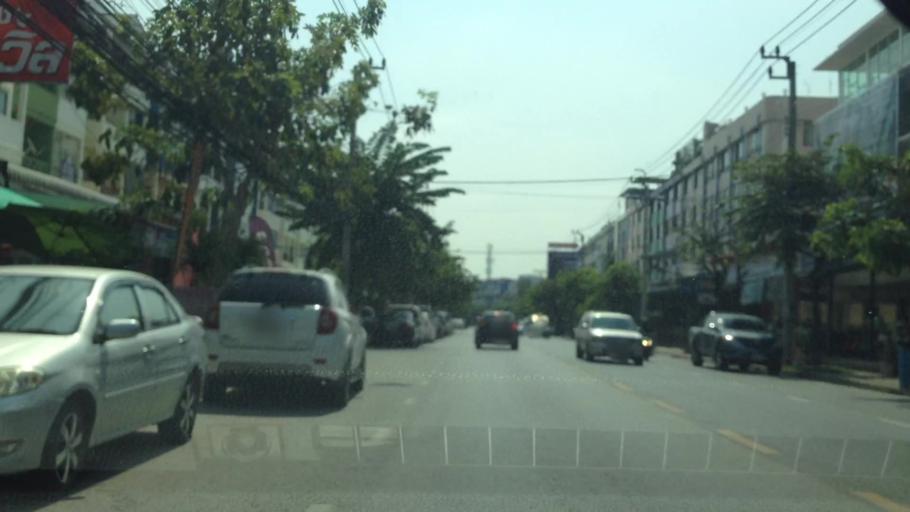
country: TH
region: Bangkok
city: Bang Khen
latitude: 13.8977
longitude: 100.6380
